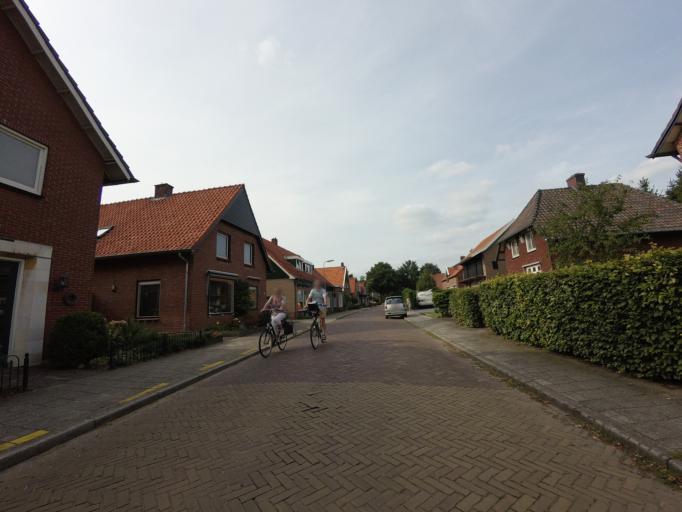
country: DE
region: Lower Saxony
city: Getelo
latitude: 52.4345
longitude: 6.8319
